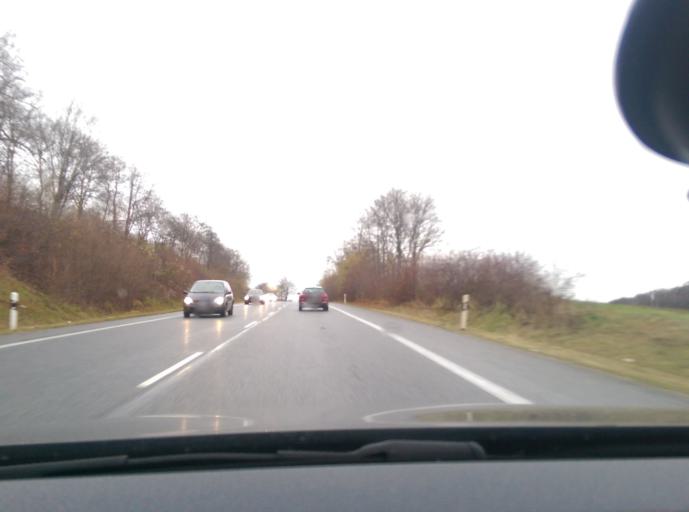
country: DE
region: Lower Saxony
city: Gemeinde Friedland
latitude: 51.3933
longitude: 9.9080
